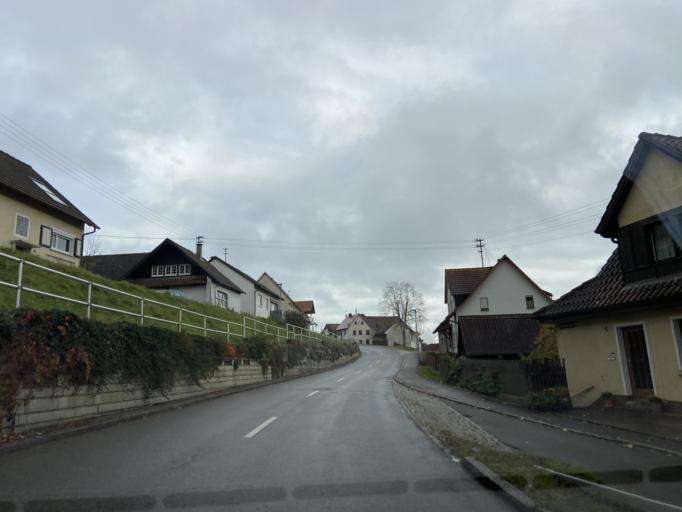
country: DE
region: Baden-Wuerttemberg
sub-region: Freiburg Region
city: Irndorf
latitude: 48.0657
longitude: 8.9672
